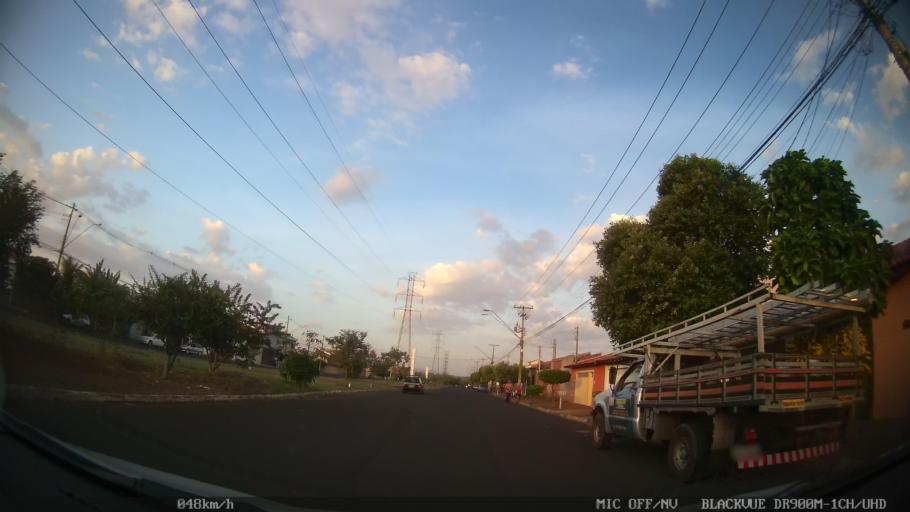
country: BR
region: Sao Paulo
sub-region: Ribeirao Preto
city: Ribeirao Preto
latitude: -21.1199
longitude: -47.8211
